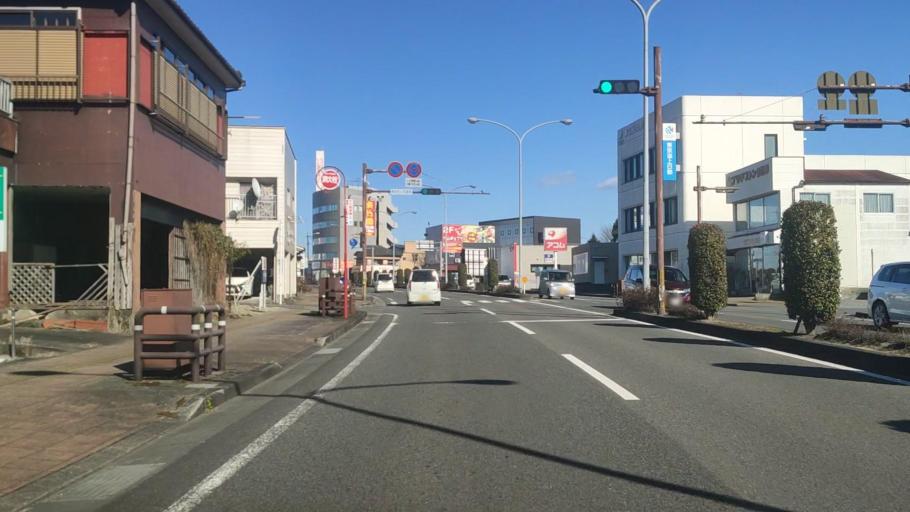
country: JP
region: Miyazaki
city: Miyakonojo
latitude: 31.7301
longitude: 131.0676
